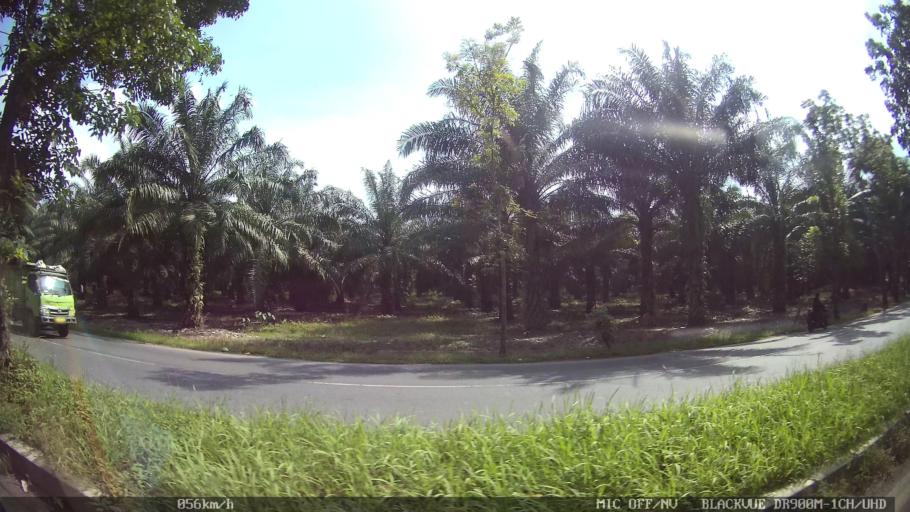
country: ID
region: North Sumatra
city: Binjai
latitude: 3.6513
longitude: 98.5336
